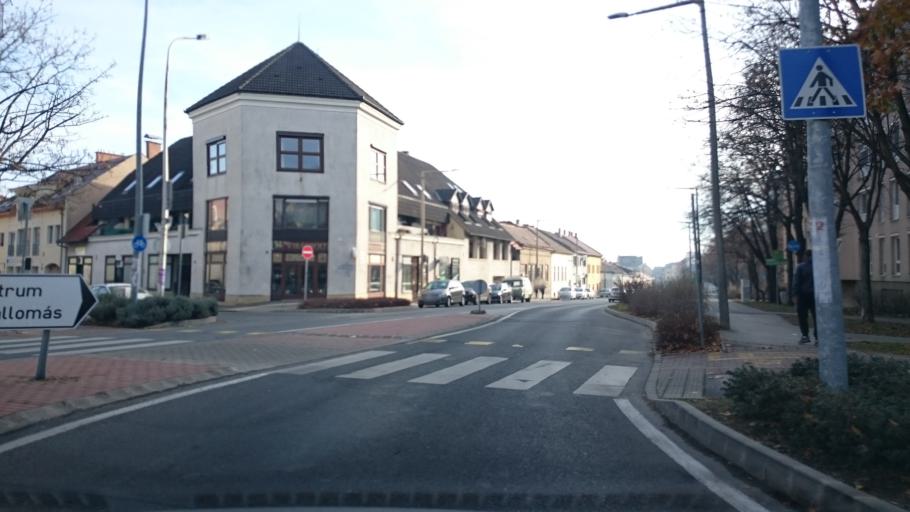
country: HU
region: Baranya
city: Pecs
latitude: 46.0770
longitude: 18.2144
